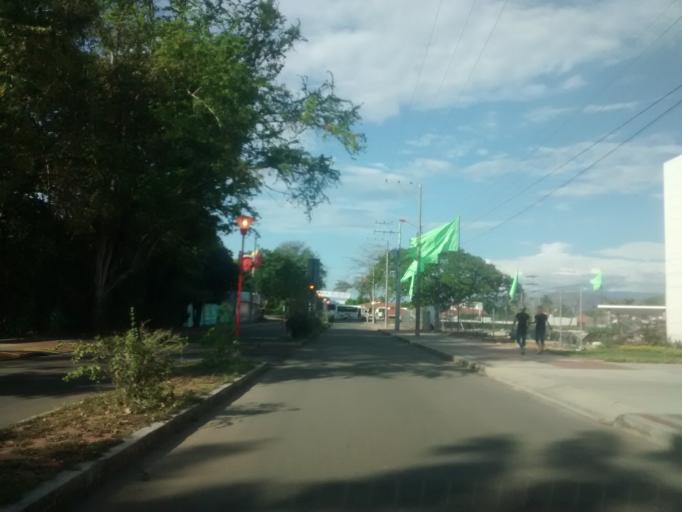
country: CO
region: Cundinamarca
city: Ricaurte
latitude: 4.2807
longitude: -74.7679
